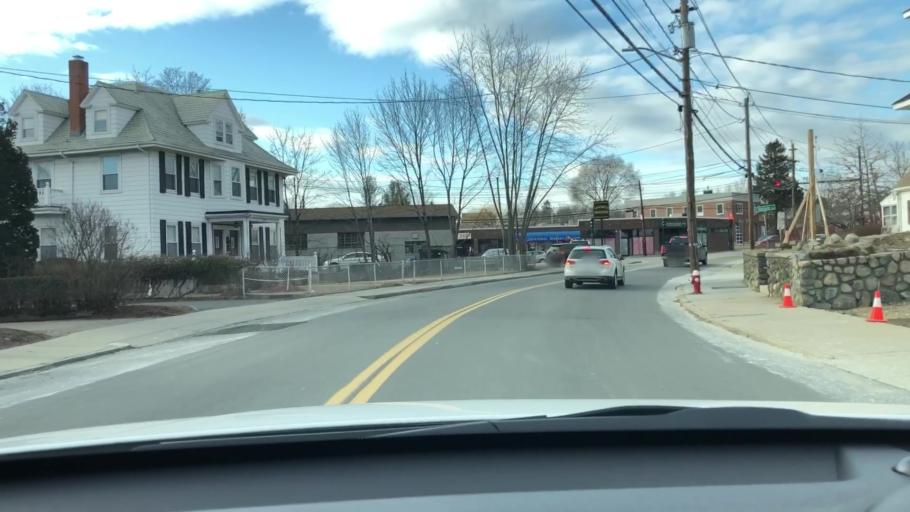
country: US
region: Massachusetts
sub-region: Middlesex County
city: Watertown
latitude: 42.3769
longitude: -71.1871
